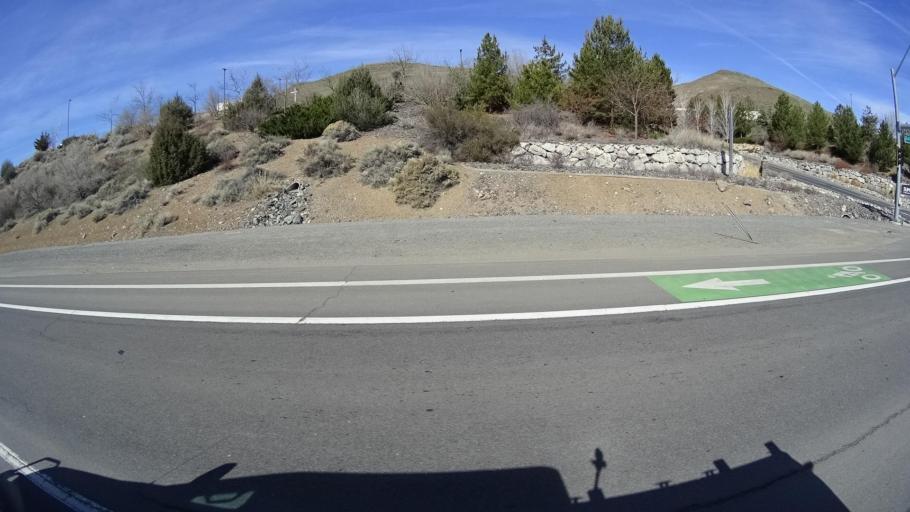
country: US
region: Nevada
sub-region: Washoe County
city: Sun Valley
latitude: 39.5936
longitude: -119.7388
